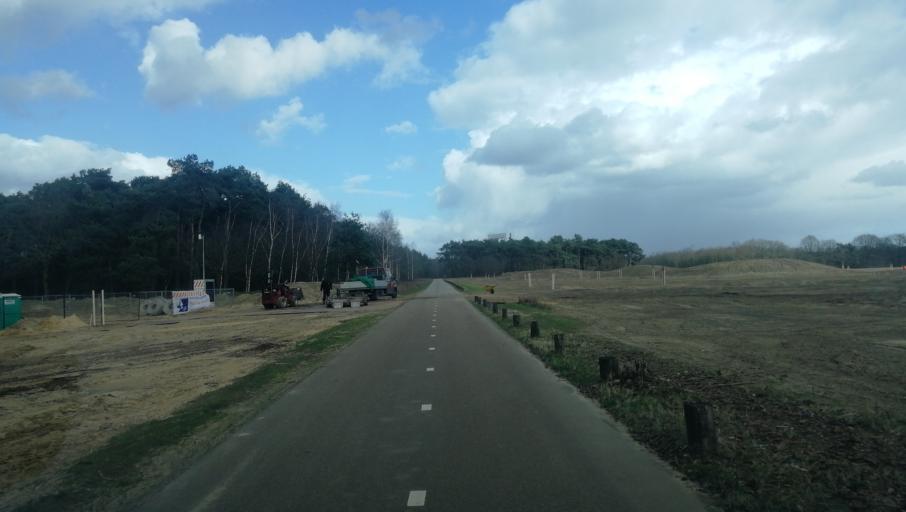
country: NL
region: Limburg
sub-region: Gemeente Venlo
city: Tegelen
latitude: 51.3986
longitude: 6.1118
